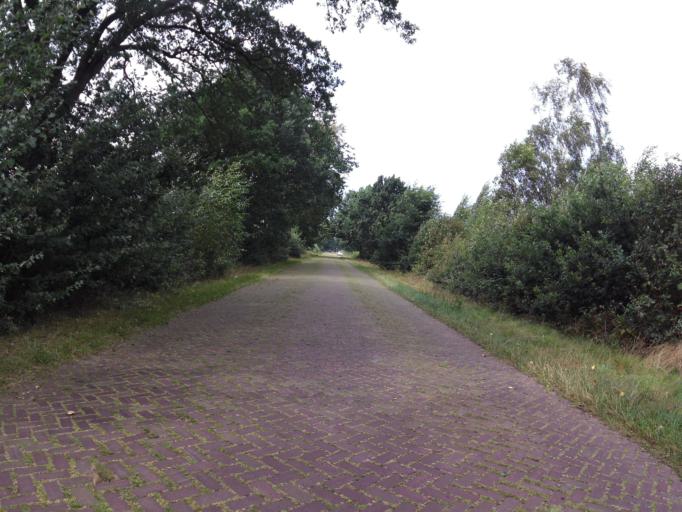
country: NL
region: Drenthe
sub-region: Gemeente Emmen
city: Klazienaveen
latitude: 52.6767
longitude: 6.9527
